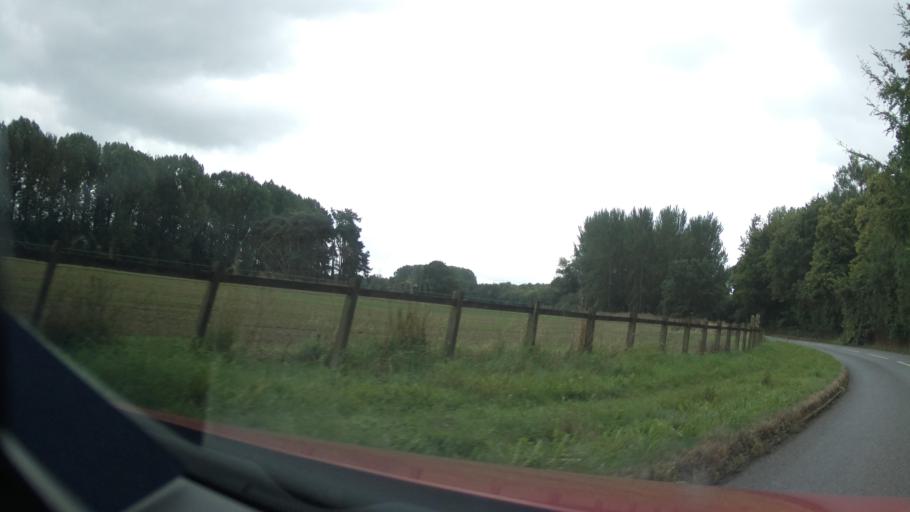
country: GB
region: England
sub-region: Staffordshire
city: Eccleshall
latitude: 52.9057
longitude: -2.2199
